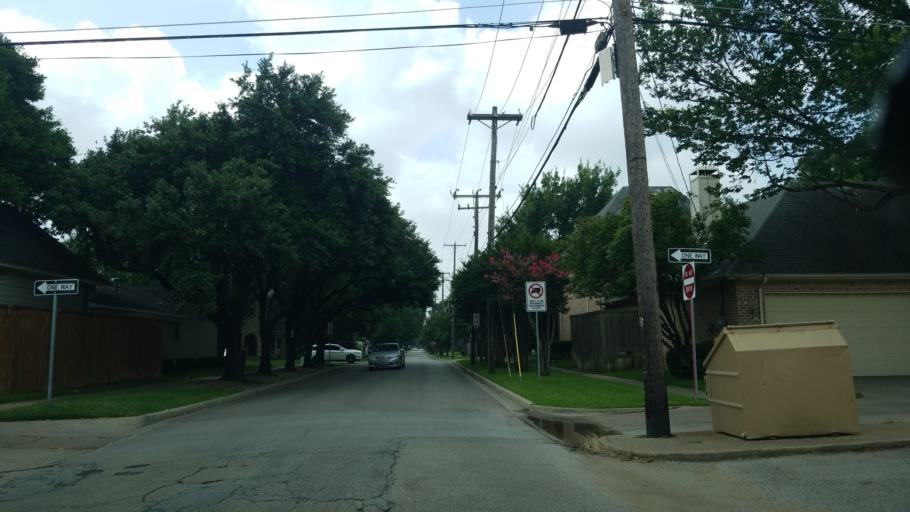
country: US
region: Texas
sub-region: Dallas County
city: University Park
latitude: 32.8508
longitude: -96.8103
